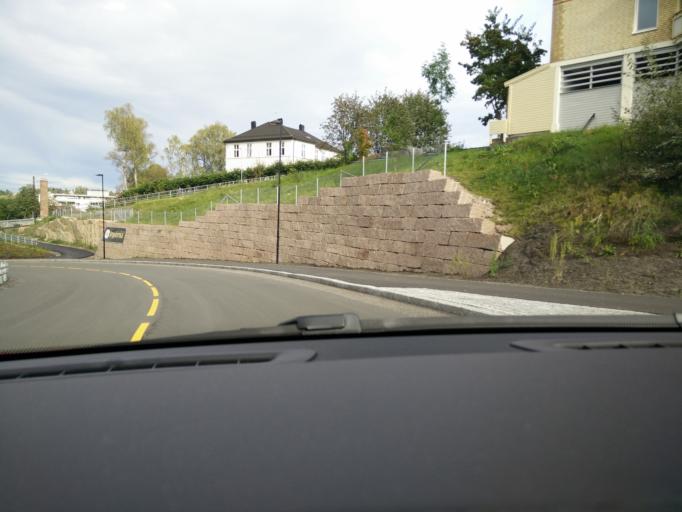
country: NO
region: Akershus
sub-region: Asker
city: Blakstad
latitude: 59.7856
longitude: 10.4316
